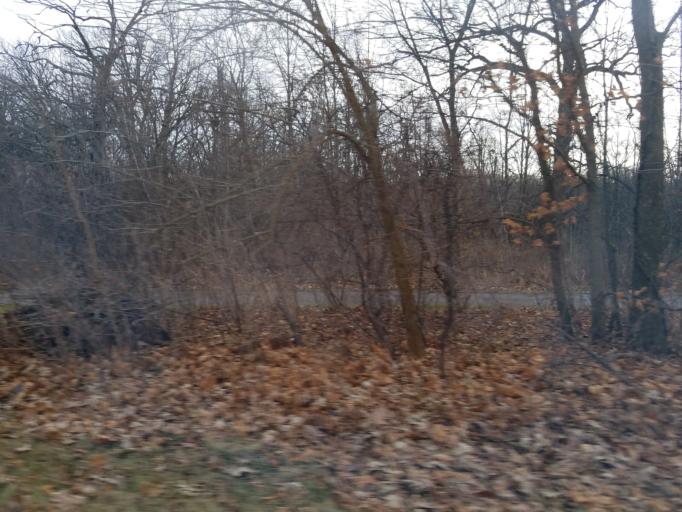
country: US
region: Illinois
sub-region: Will County
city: Mokena
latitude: 41.5280
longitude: -87.8672
